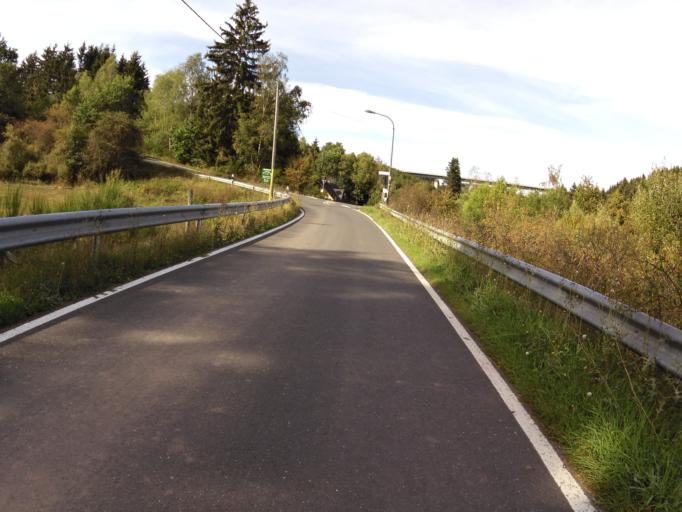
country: DE
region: Rheinland-Pfalz
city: Habscheid
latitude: 50.1947
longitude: 6.2860
